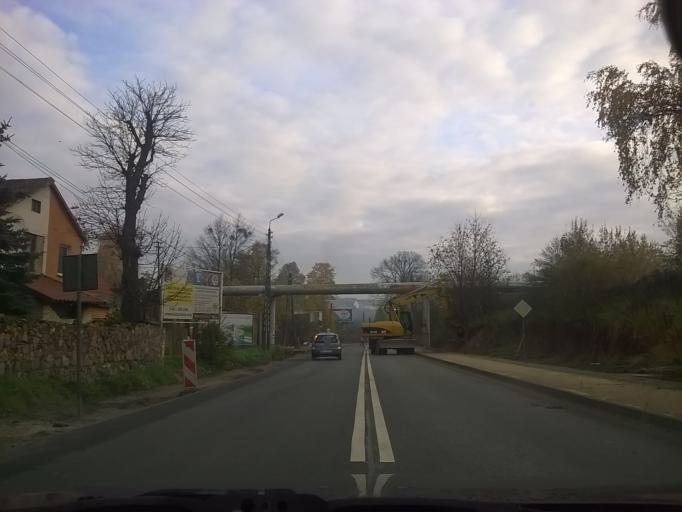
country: PL
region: Pomeranian Voivodeship
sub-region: Gdansk
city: Gdansk
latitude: 54.3296
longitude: 18.6191
